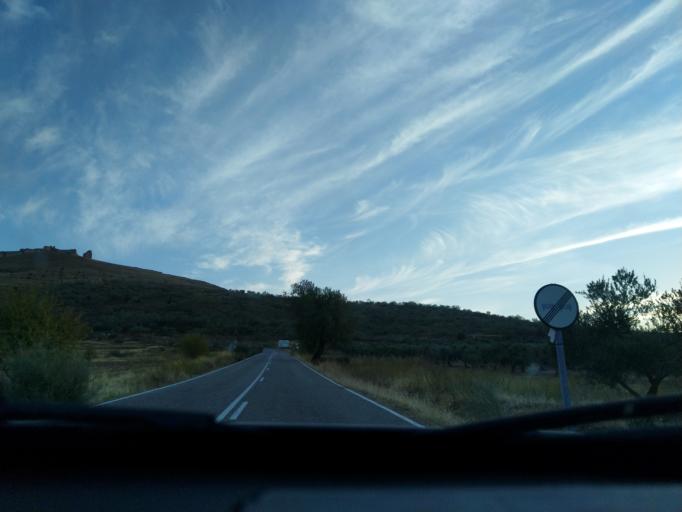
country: ES
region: Extremadura
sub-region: Provincia de Badajoz
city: Casas de Reina
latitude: 38.1978
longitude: -5.9555
